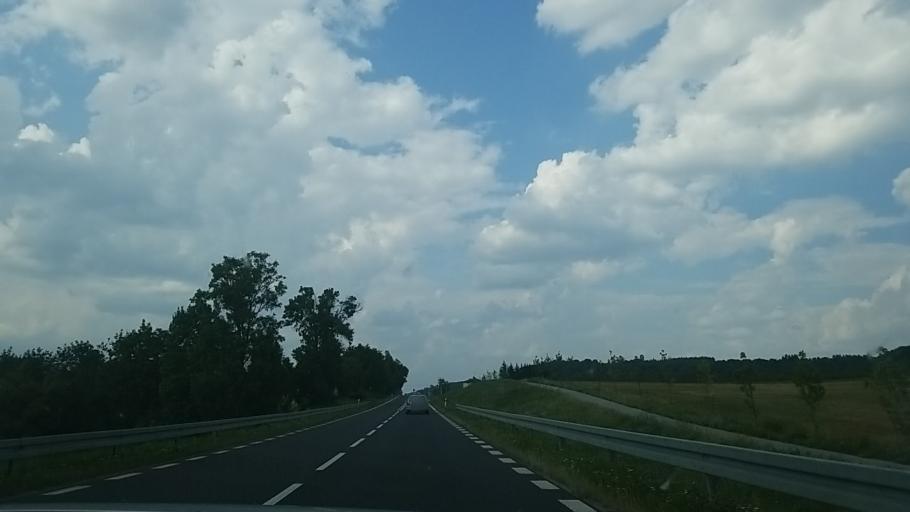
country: PL
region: Lublin Voivodeship
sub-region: Powiat bilgorajski
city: Goraj
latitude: 50.7347
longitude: 22.6680
